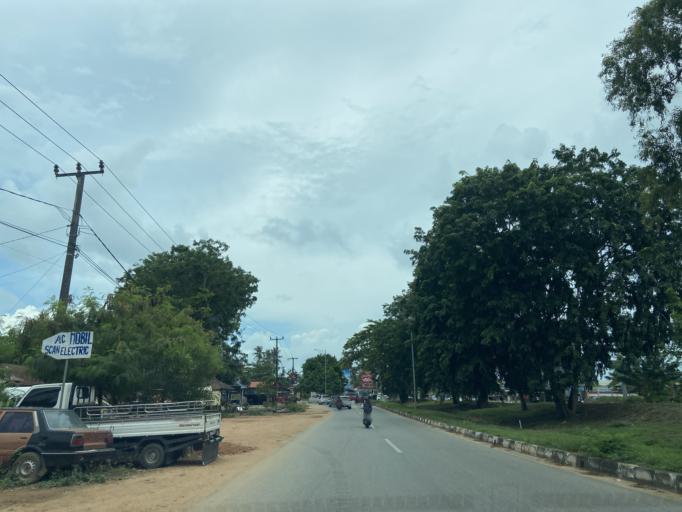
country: SG
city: Singapore
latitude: 1.1483
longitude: 104.1314
